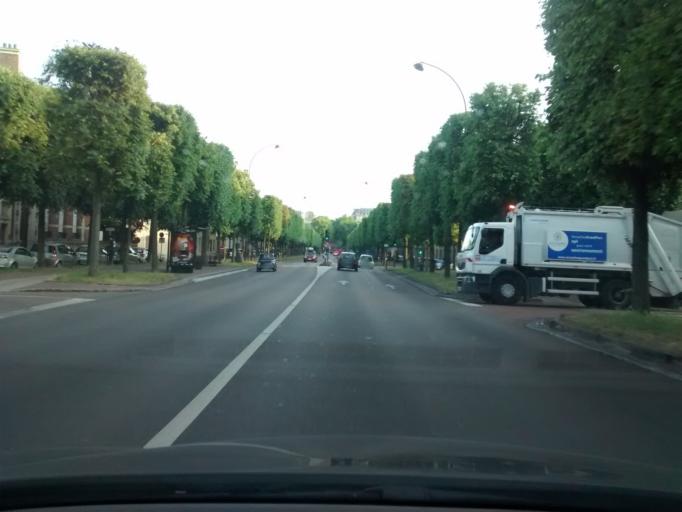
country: FR
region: Ile-de-France
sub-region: Departement des Yvelines
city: Le Chesnay
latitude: 48.8124
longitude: 2.1272
